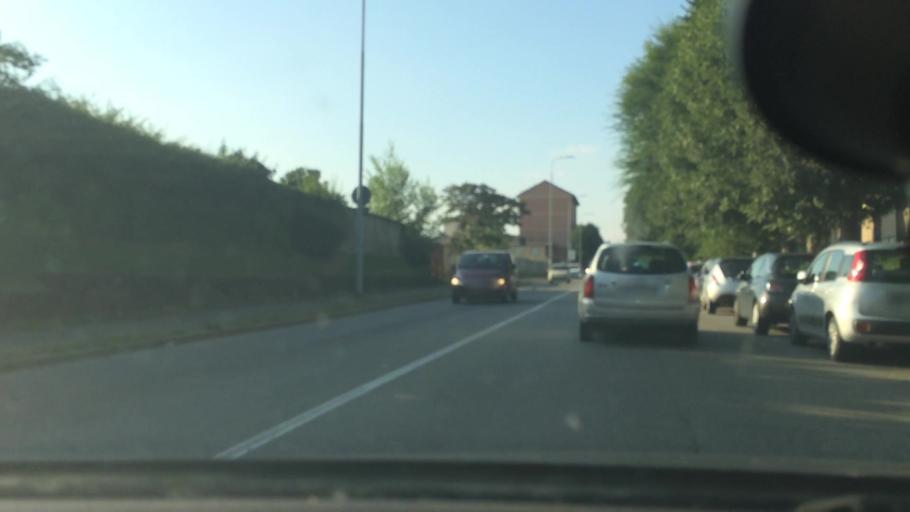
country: IT
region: Lombardy
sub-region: Citta metropolitana di Milano
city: Rho
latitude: 45.5262
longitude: 9.0466
